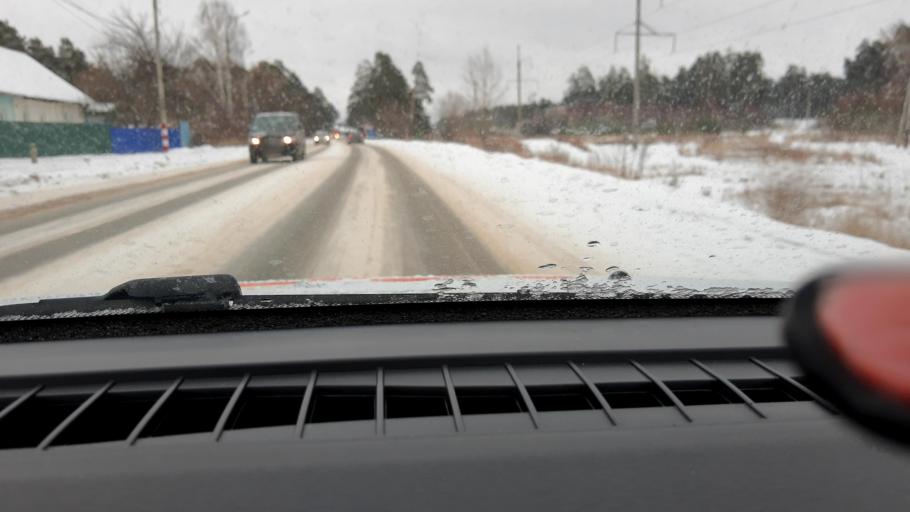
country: RU
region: Nizjnij Novgorod
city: Bor
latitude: 56.3303
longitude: 44.1195
